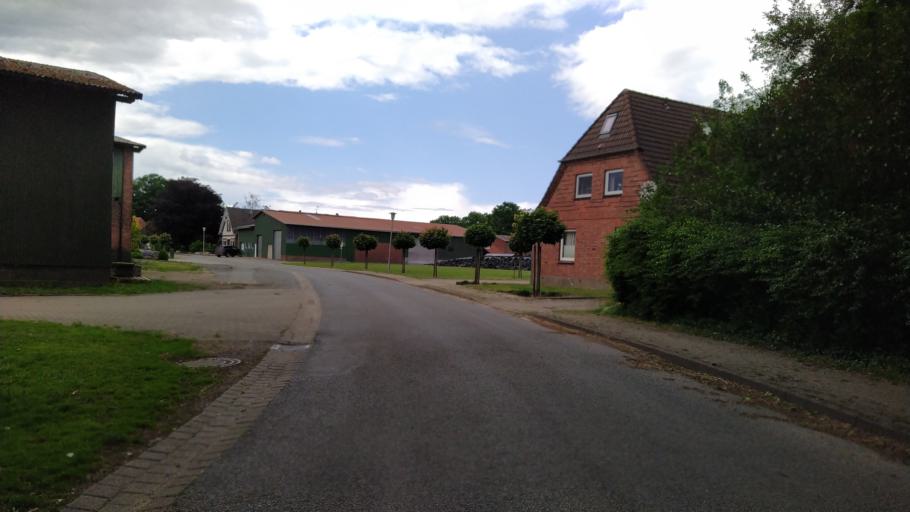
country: DE
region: Lower Saxony
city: Brest
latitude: 53.4627
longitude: 9.3777
